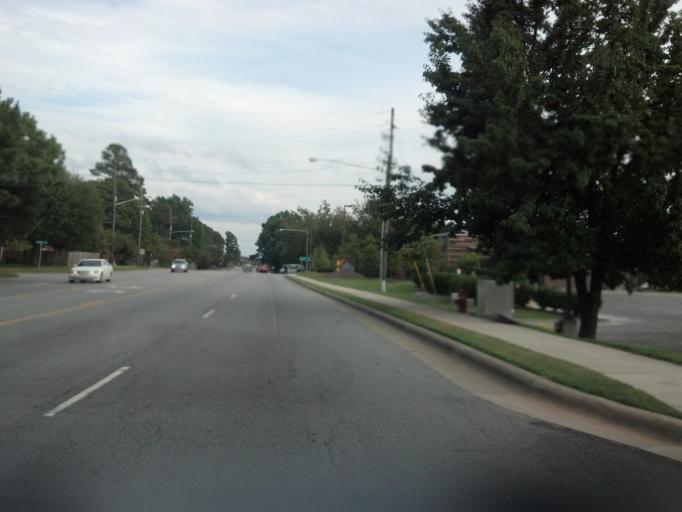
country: US
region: North Carolina
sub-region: Pitt County
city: Greenville
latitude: 35.5880
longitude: -77.3664
